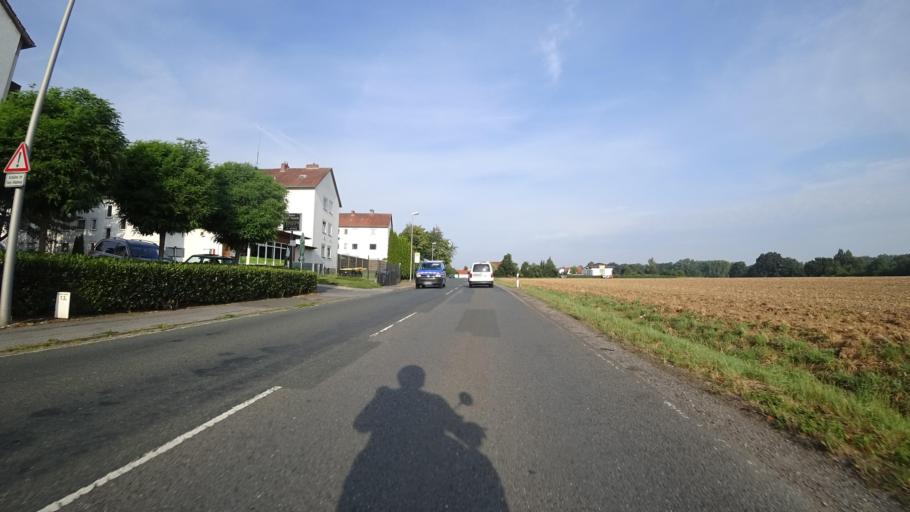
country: DE
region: North Rhine-Westphalia
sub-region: Regierungsbezirk Detmold
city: Bielefeld
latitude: 52.0591
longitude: 8.5134
